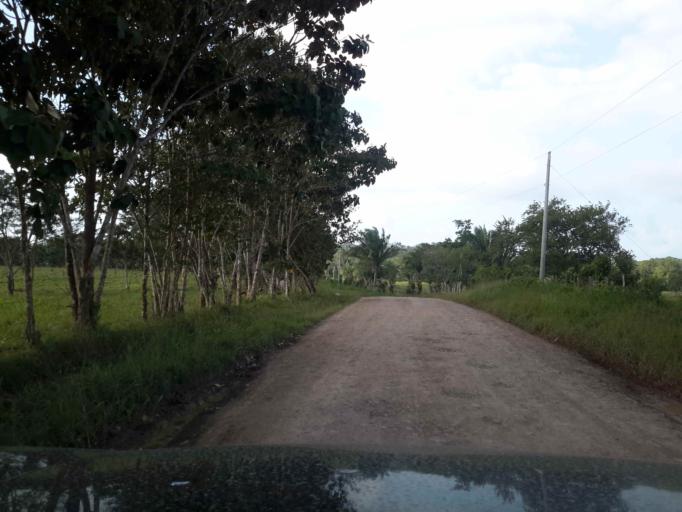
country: CR
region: Alajuela
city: Los Chiles
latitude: 11.1302
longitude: -84.6080
